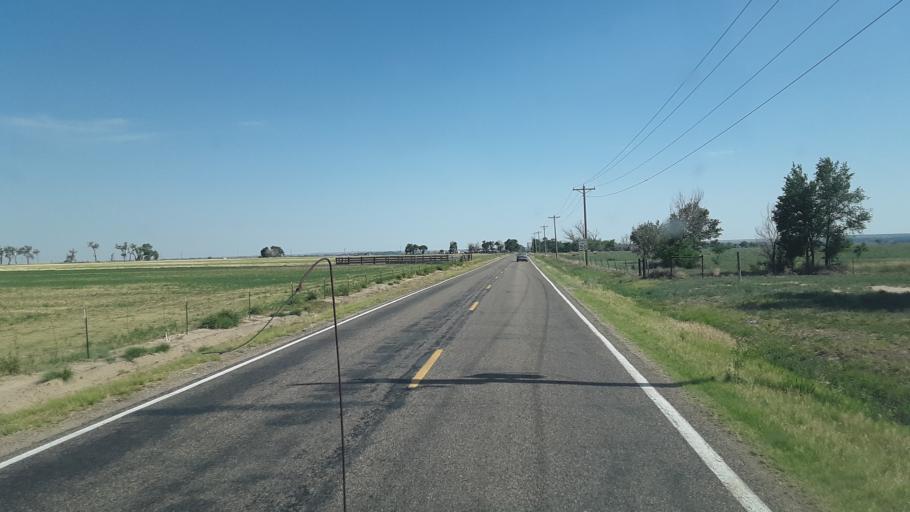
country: US
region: Colorado
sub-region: Crowley County
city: Ordway
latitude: 38.1629
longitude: -103.8571
